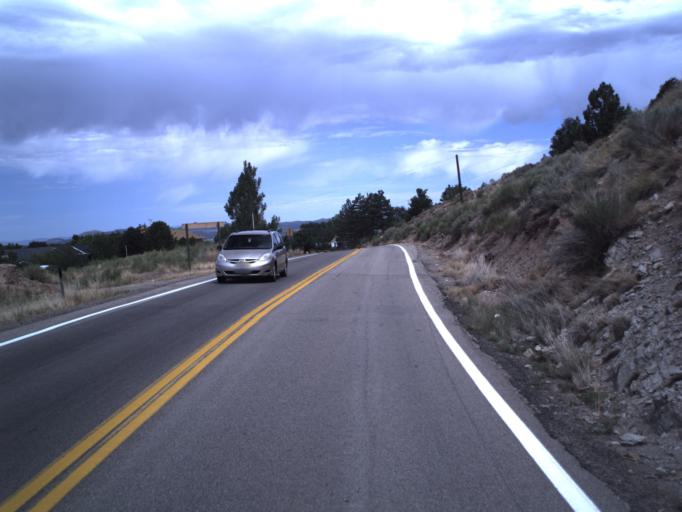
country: US
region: Utah
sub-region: Iron County
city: Cedar City
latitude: 37.6758
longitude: -113.0505
